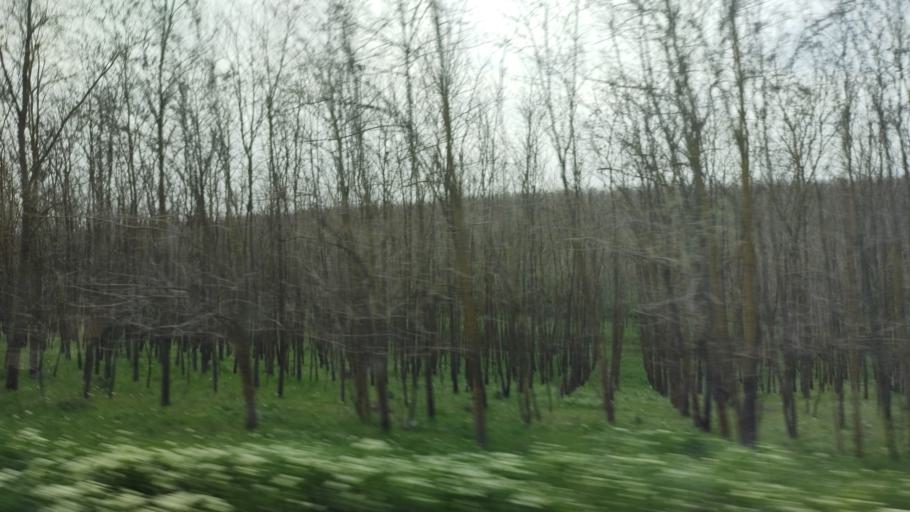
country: RO
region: Constanta
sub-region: Comuna Deleni
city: Pietreni
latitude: 44.0898
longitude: 28.0854
